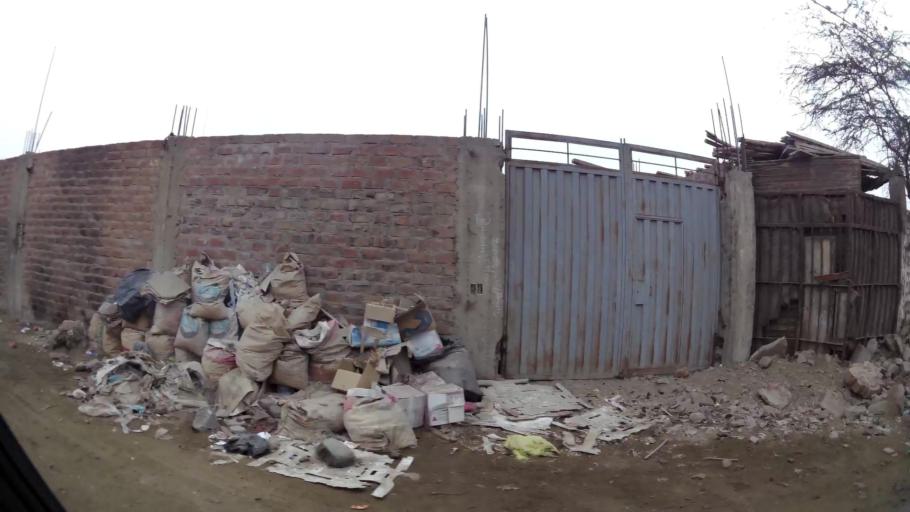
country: PE
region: Lima
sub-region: Lima
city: Urb. Santo Domingo
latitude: -11.9000
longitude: -77.0640
